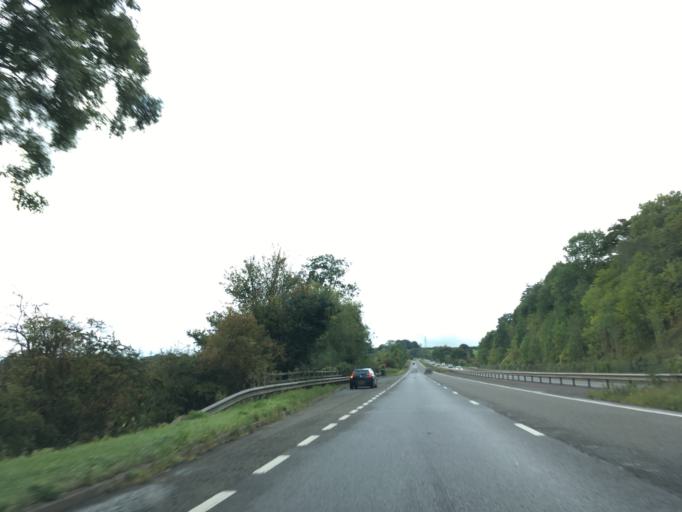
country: GB
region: England
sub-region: Herefordshire
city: Walford
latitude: 51.8986
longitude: -2.6296
